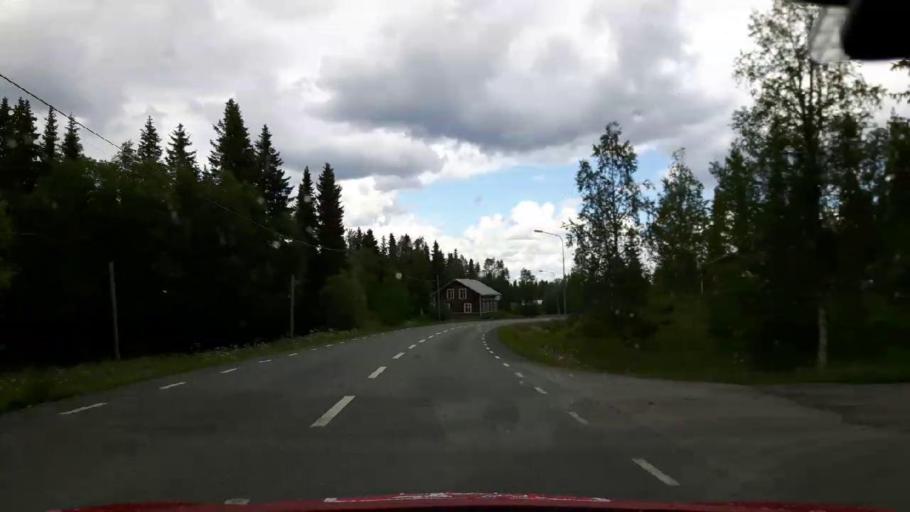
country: SE
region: Jaemtland
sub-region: Krokoms Kommun
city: Krokom
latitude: 63.7561
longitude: 14.3031
